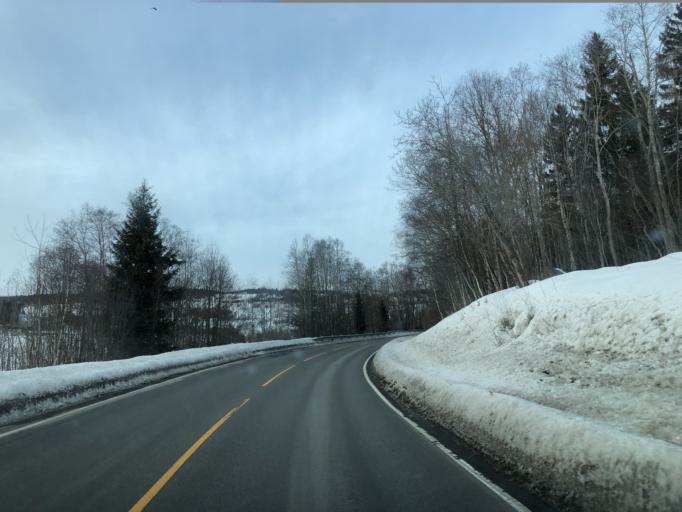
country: NO
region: Oppland
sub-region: Gausdal
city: Segalstad bru
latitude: 61.2747
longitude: 10.1460
